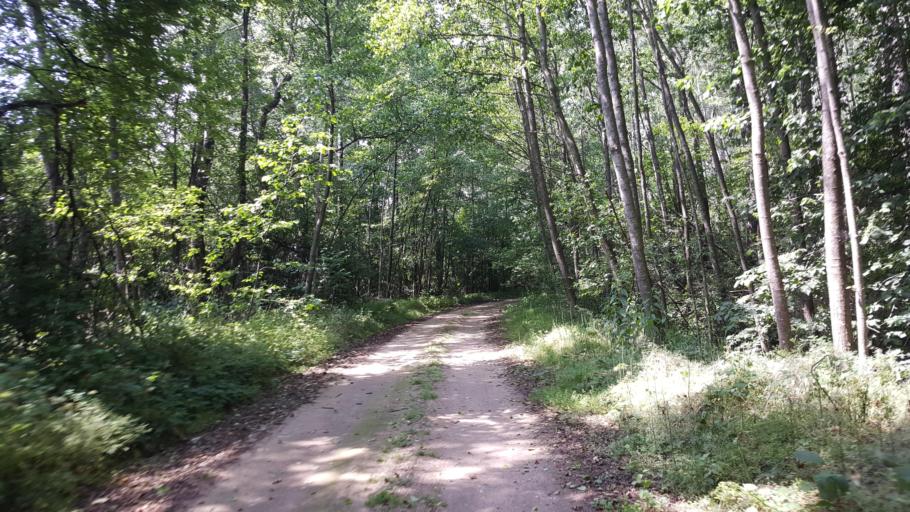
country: BY
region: Brest
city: Kamyanyets
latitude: 52.3663
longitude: 23.7532
